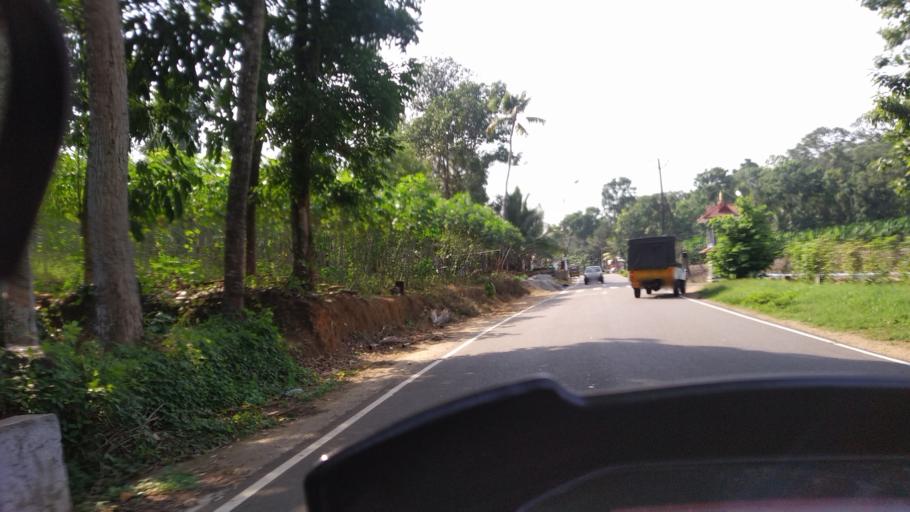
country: IN
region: Kerala
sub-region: Ernakulam
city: Piravam
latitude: 9.8111
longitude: 76.5703
